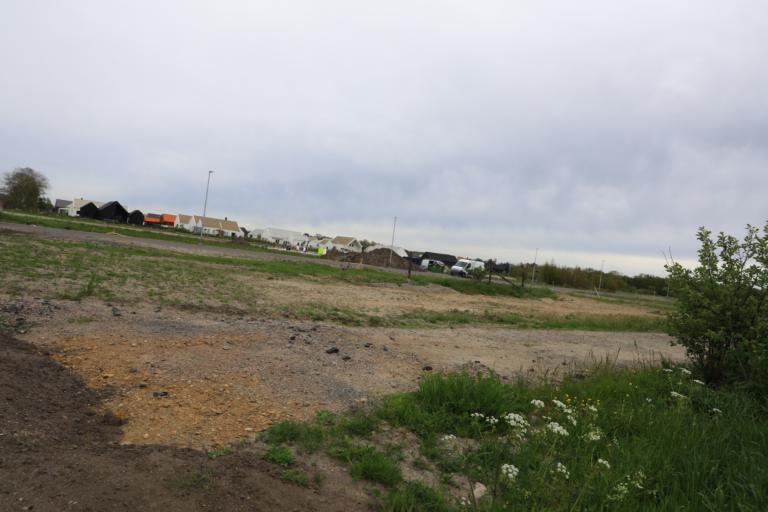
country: SE
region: Halland
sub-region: Varbergs Kommun
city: Varberg
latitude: 57.1470
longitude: 12.2333
